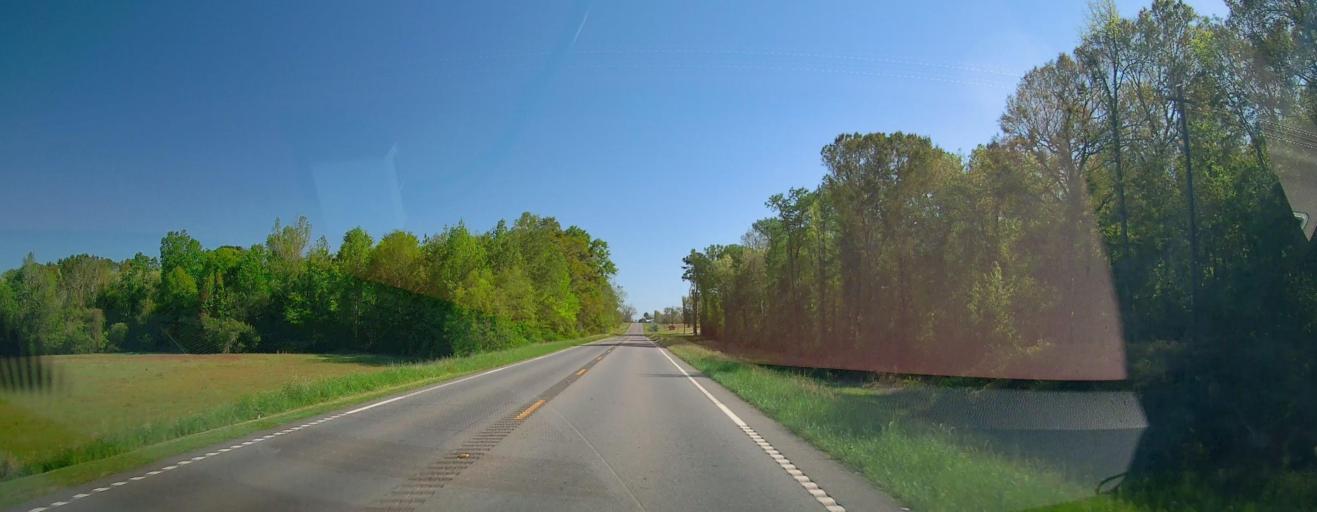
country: US
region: Georgia
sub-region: Pulaski County
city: Hawkinsville
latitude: 32.1206
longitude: -83.5008
